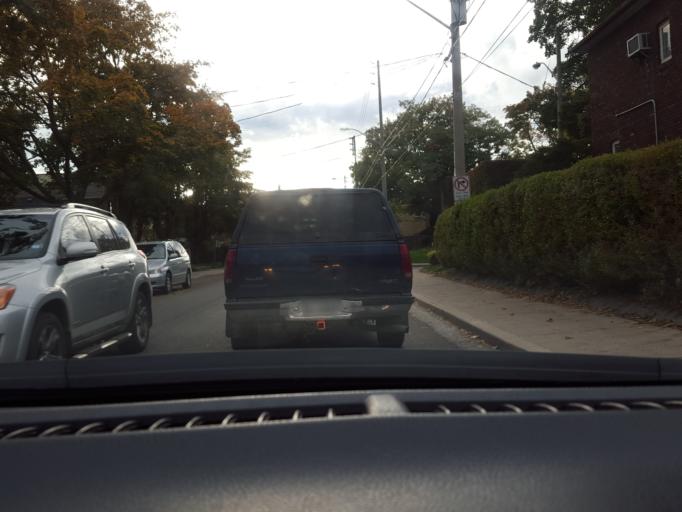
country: CA
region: Ontario
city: Toronto
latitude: 43.7046
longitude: -79.3730
